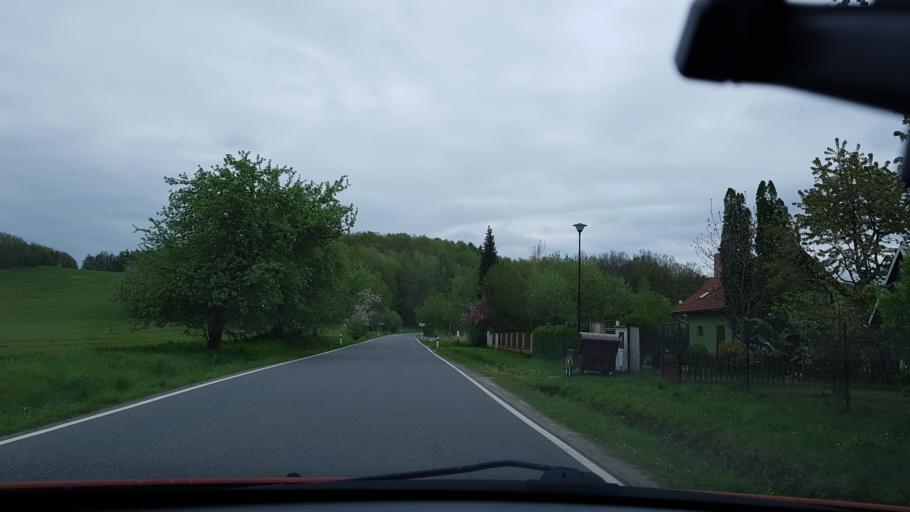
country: CZ
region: Olomoucky
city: Vidnava
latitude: 50.3704
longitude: 17.1903
